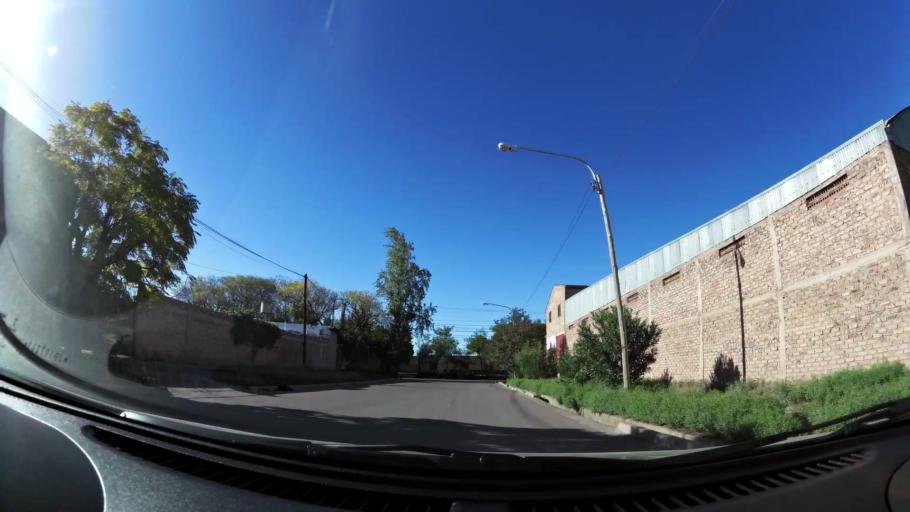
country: AR
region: Mendoza
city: Las Heras
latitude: -32.8426
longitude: -68.8166
